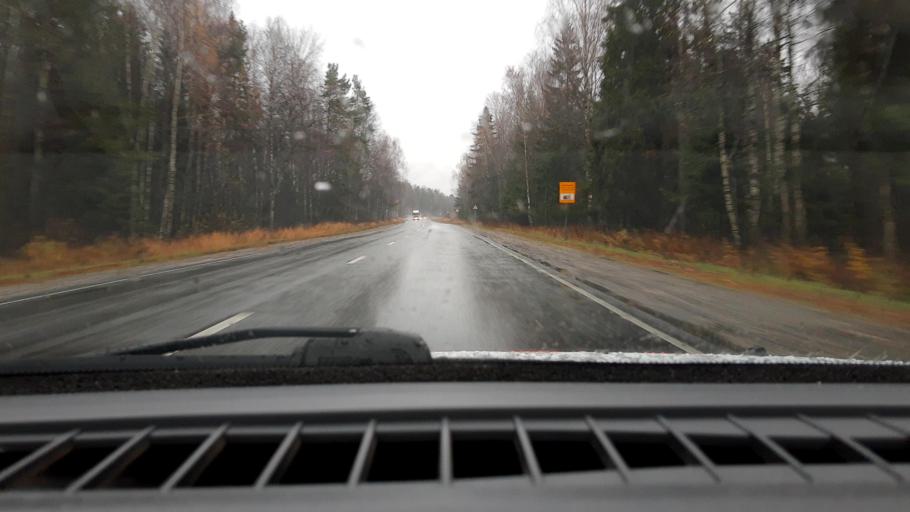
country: RU
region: Nizjnij Novgorod
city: Linda
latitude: 56.6296
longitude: 44.0892
